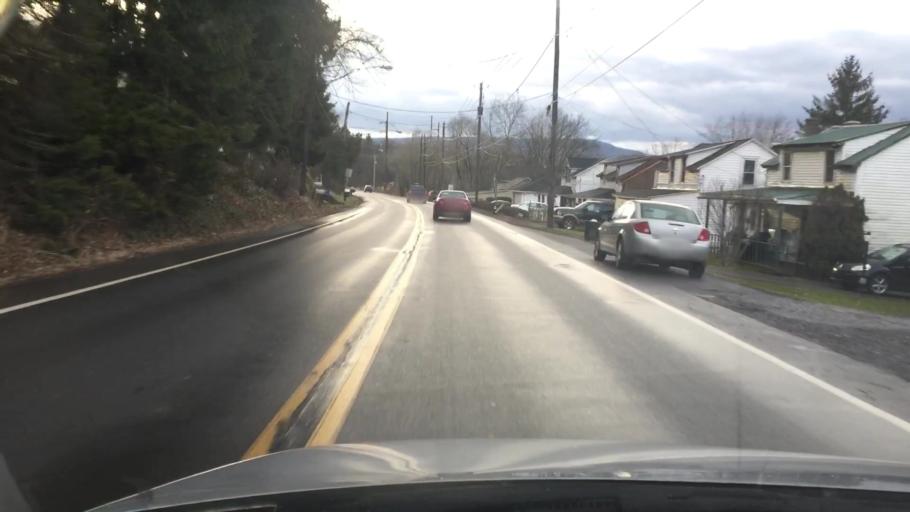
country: US
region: Pennsylvania
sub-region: Columbia County
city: Bloomsburg
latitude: 41.0114
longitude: -76.4658
